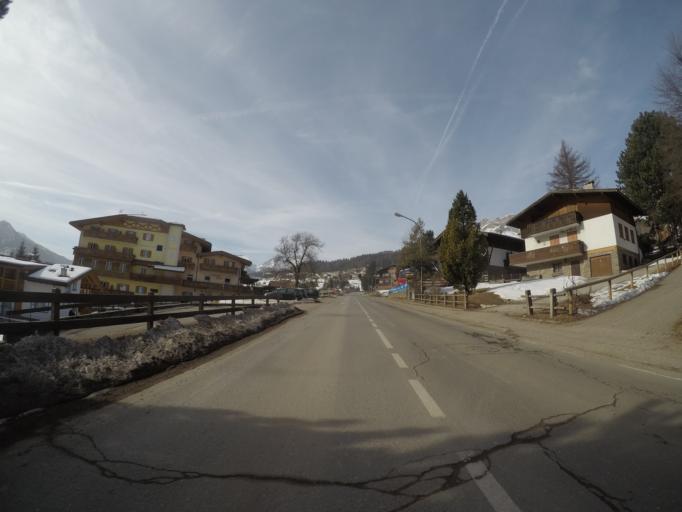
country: IT
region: Trentino-Alto Adige
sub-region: Provincia di Trento
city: Vigo di Fassa
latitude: 46.4187
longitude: 11.6782
